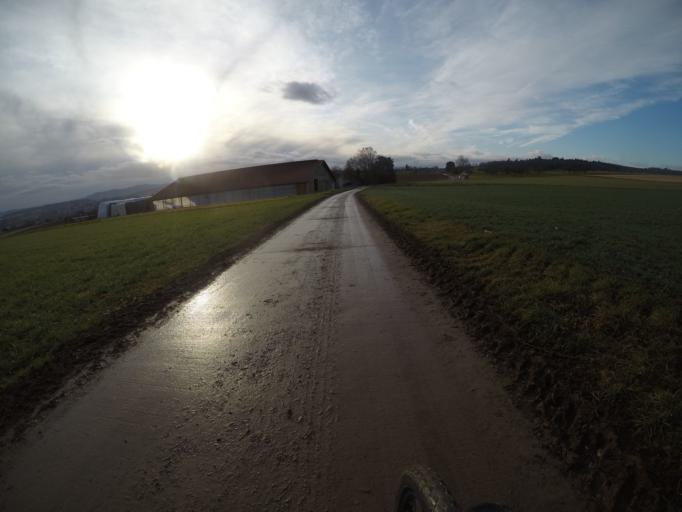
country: DE
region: Baden-Wuerttemberg
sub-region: Regierungsbezirk Stuttgart
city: Unterensingen
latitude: 48.6656
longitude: 9.3426
